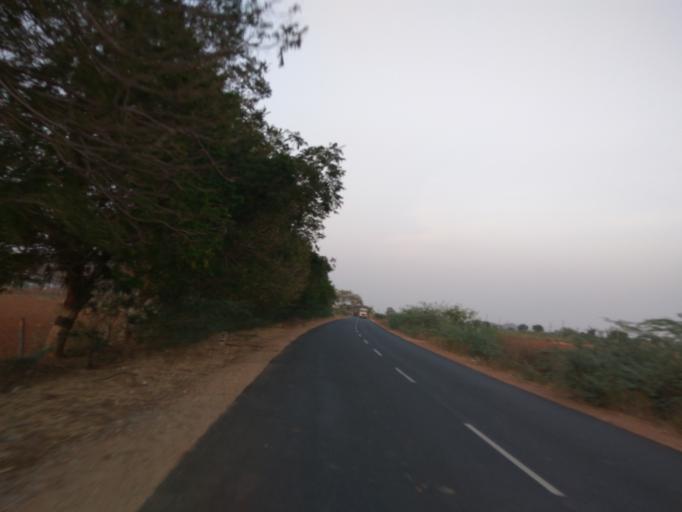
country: IN
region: Andhra Pradesh
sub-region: Prakasam
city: Markapur
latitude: 15.7512
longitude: 79.2197
